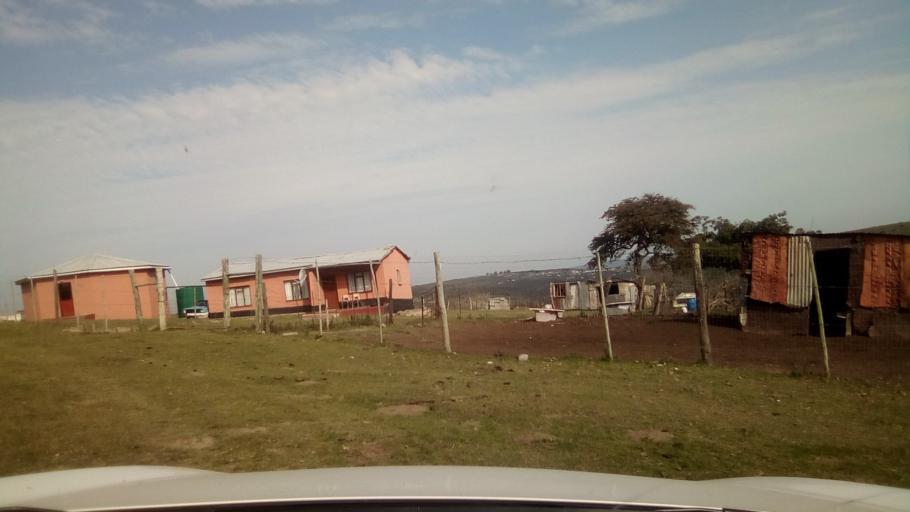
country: ZA
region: Eastern Cape
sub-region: Buffalo City Metropolitan Municipality
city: Bhisho
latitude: -33.0091
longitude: 27.3043
